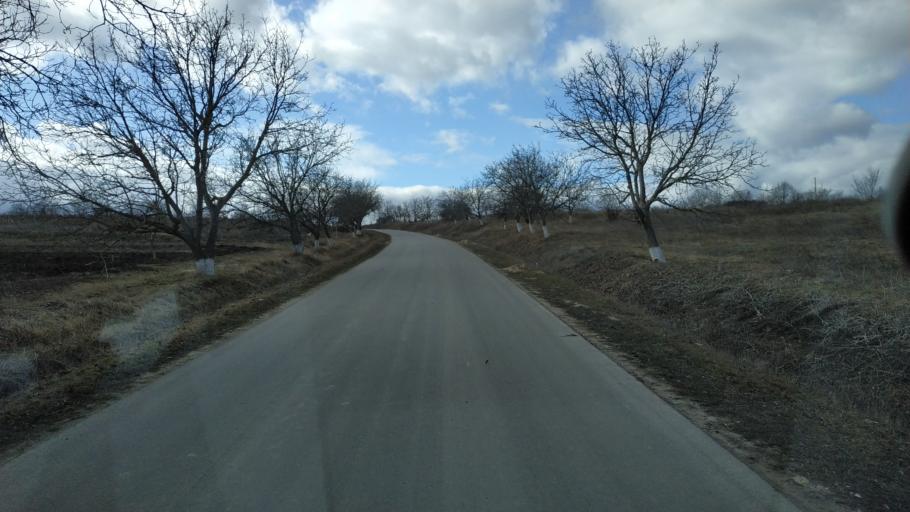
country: MD
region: Stinga Nistrului
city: Bucovat
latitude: 47.2029
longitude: 28.4944
